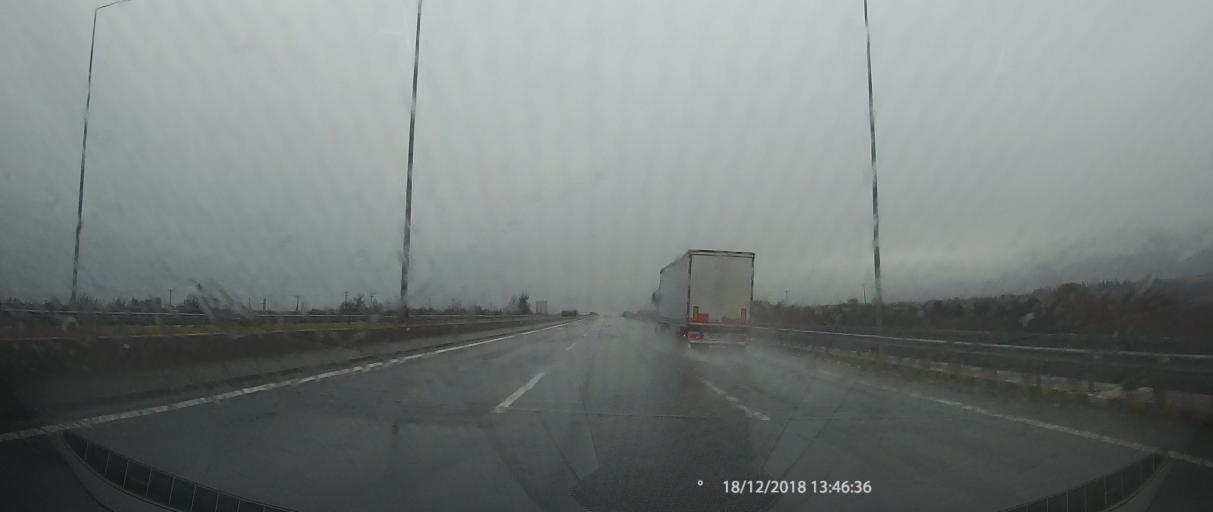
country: GR
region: Central Macedonia
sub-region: Nomos Pierias
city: Leptokarya
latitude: 40.0943
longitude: 22.5551
